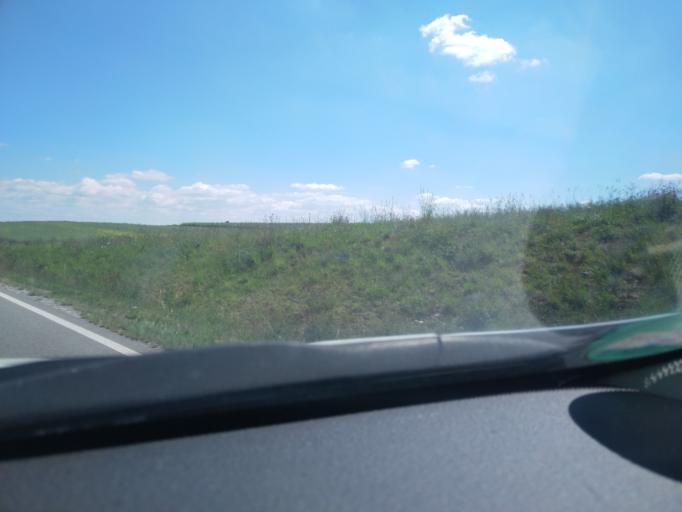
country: DE
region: Baden-Wuerttemberg
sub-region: Freiburg Region
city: Dunningen
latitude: 48.2137
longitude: 8.5300
